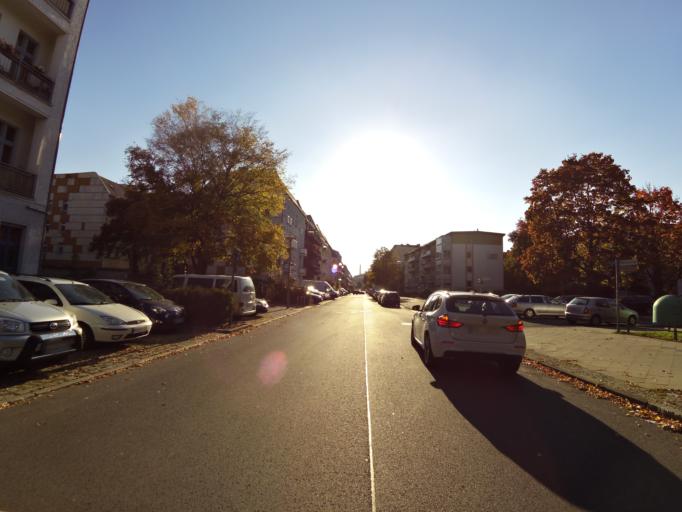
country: DE
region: Berlin
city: Oberschoneweide
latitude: 52.4608
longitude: 13.5307
